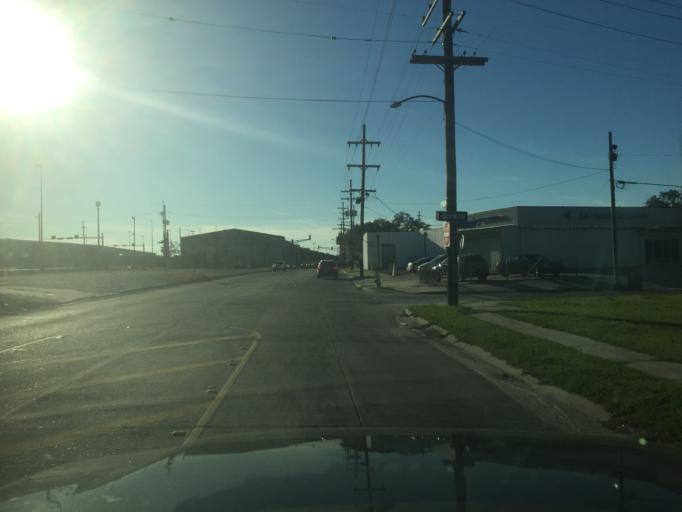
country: US
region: Louisiana
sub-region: Jefferson Parish
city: Harvey
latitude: 29.9186
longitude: -90.0851
